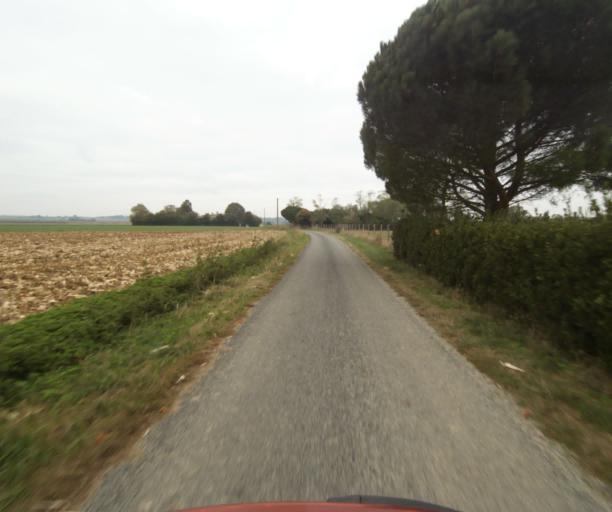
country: FR
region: Midi-Pyrenees
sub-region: Departement du Tarn-et-Garonne
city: Verdun-sur-Garonne
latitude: 43.8127
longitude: 1.2331
